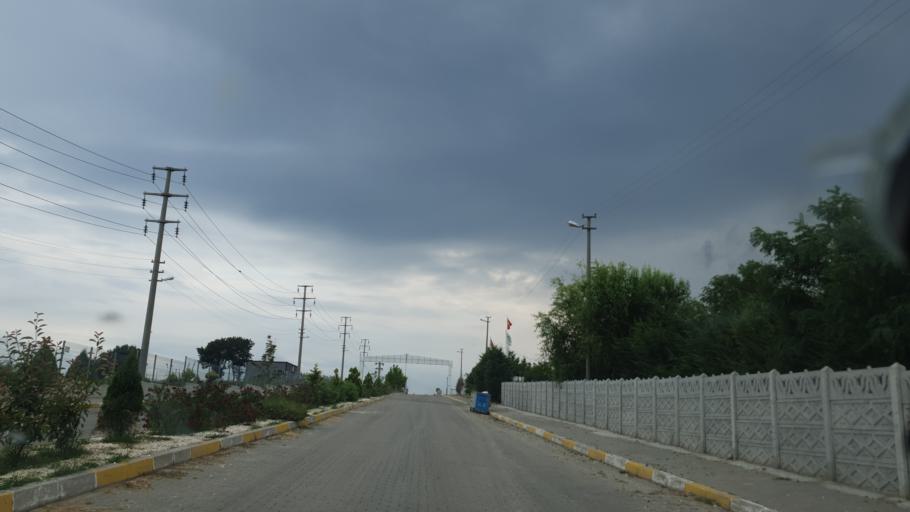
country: TR
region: Tekirdag
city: Hayrabolu
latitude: 41.2234
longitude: 27.0469
